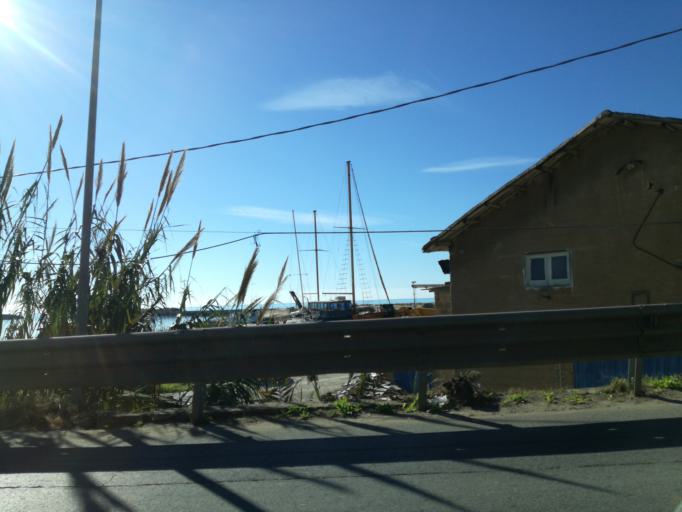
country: IT
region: Sicily
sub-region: Provincia di Caltanissetta
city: Gela
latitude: 37.0684
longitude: 14.2290
